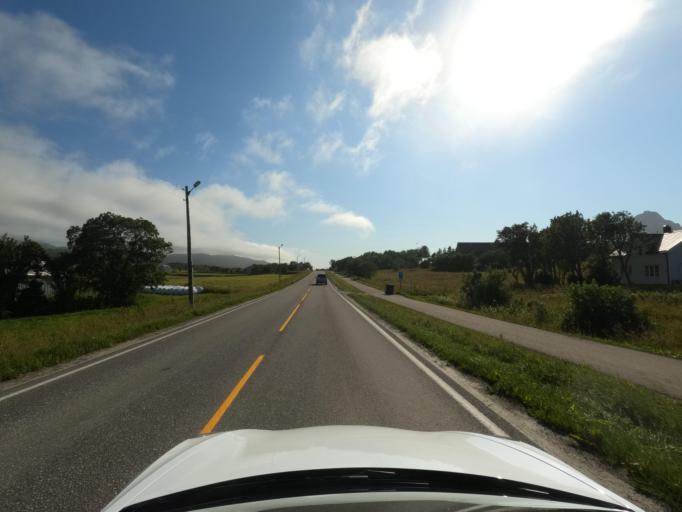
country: NO
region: Nordland
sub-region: Vestvagoy
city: Evjen
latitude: 68.2325
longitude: 13.7408
